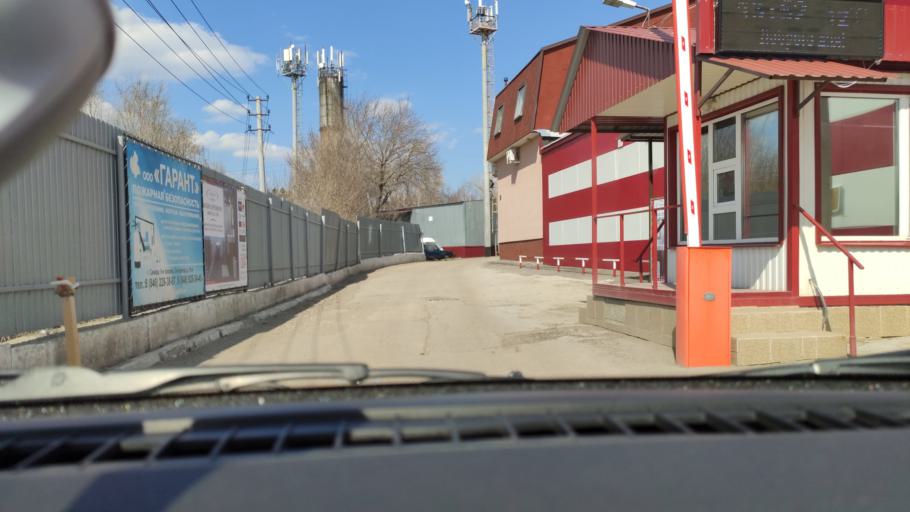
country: RU
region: Samara
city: Samara
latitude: 53.2693
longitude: 50.1880
